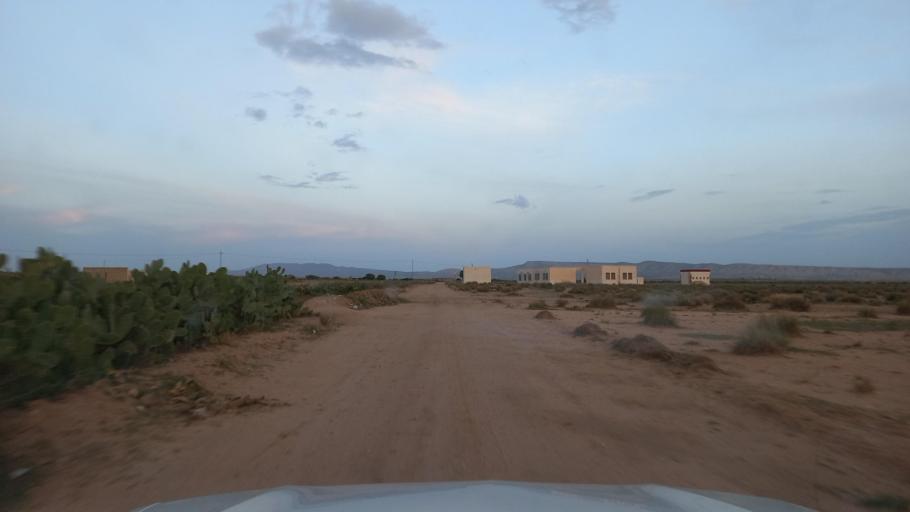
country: TN
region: Al Qasrayn
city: Sbiba
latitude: 35.3492
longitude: 9.0374
